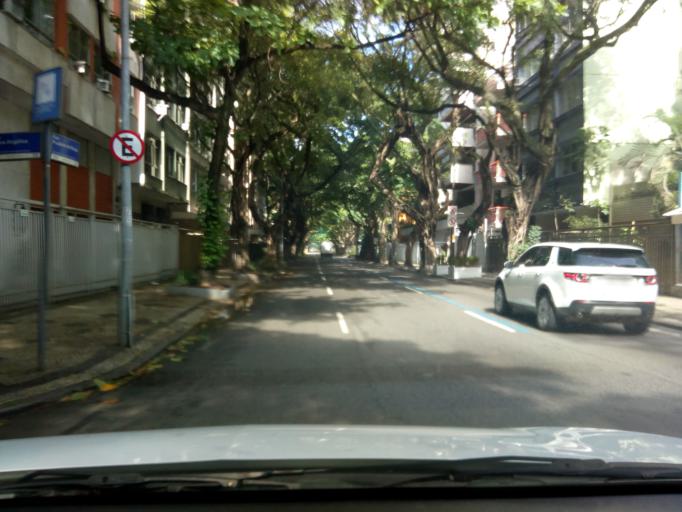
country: BR
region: Rio de Janeiro
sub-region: Rio De Janeiro
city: Rio de Janeiro
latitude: -22.9853
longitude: -43.2049
